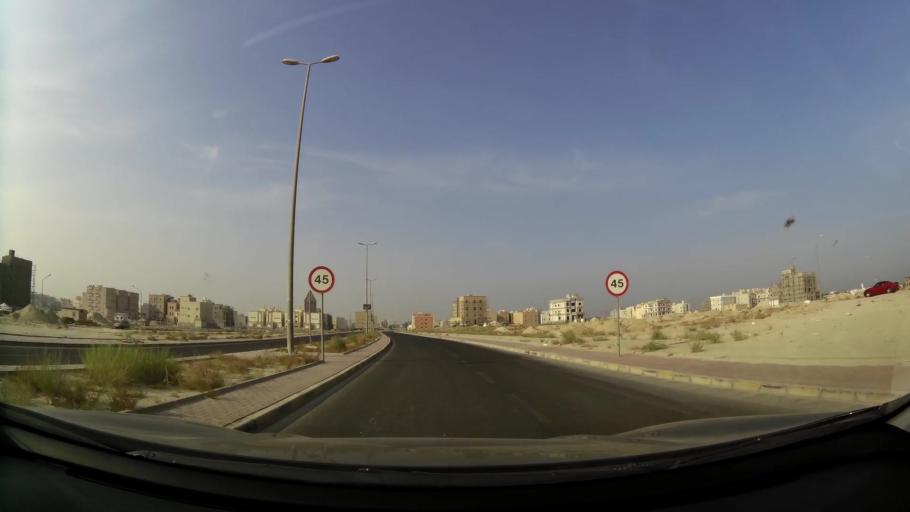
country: KW
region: Mubarak al Kabir
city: Mubarak al Kabir
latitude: 29.2003
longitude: 48.1013
